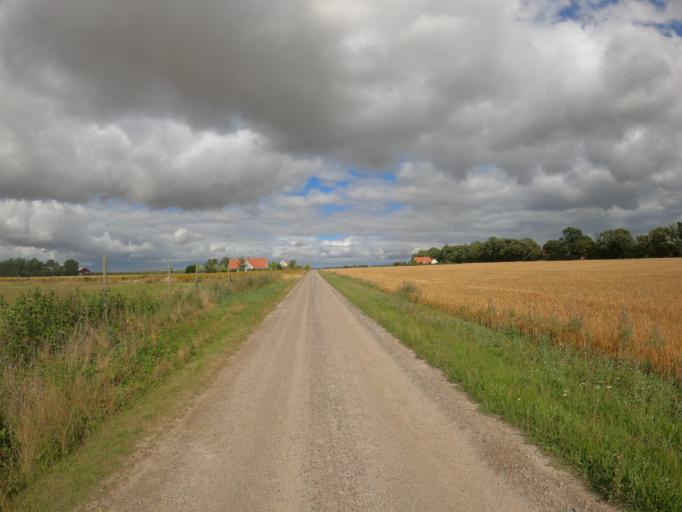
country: SE
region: Skane
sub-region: Lunds Kommun
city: Lund
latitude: 55.7315
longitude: 13.2766
